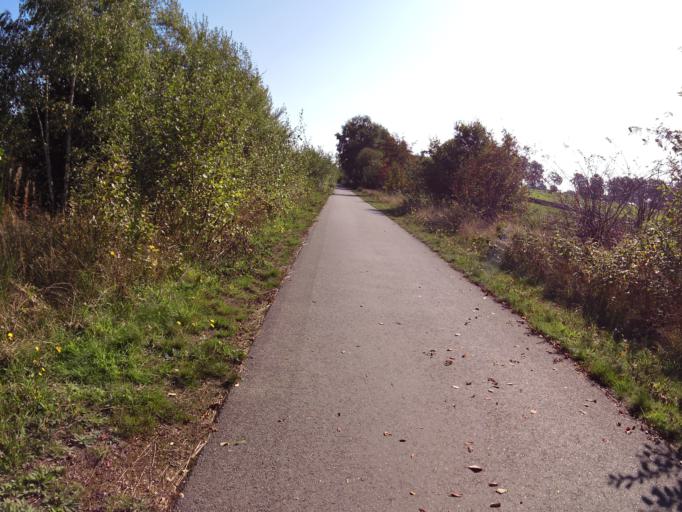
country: BE
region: Wallonia
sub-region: Province de Liege
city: Waimes
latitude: 50.4104
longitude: 6.1253
